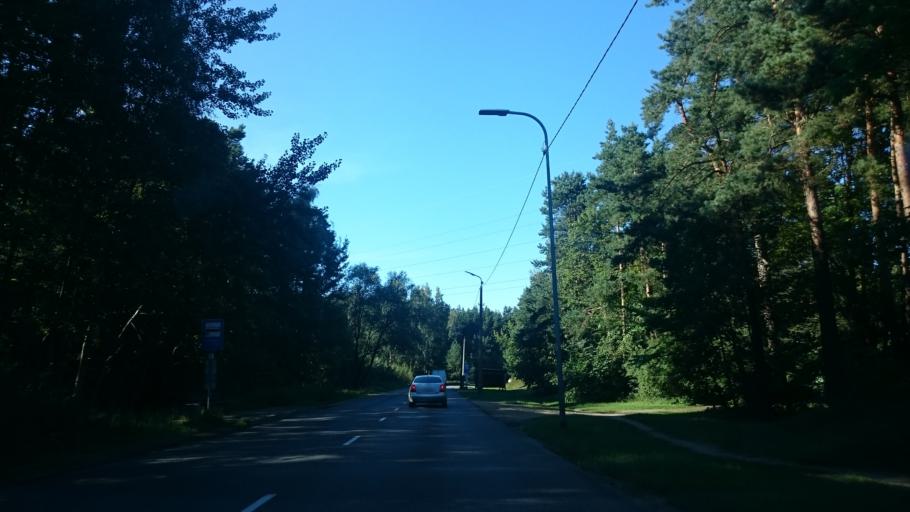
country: LV
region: Riga
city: Bolderaja
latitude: 57.0387
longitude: 24.1134
